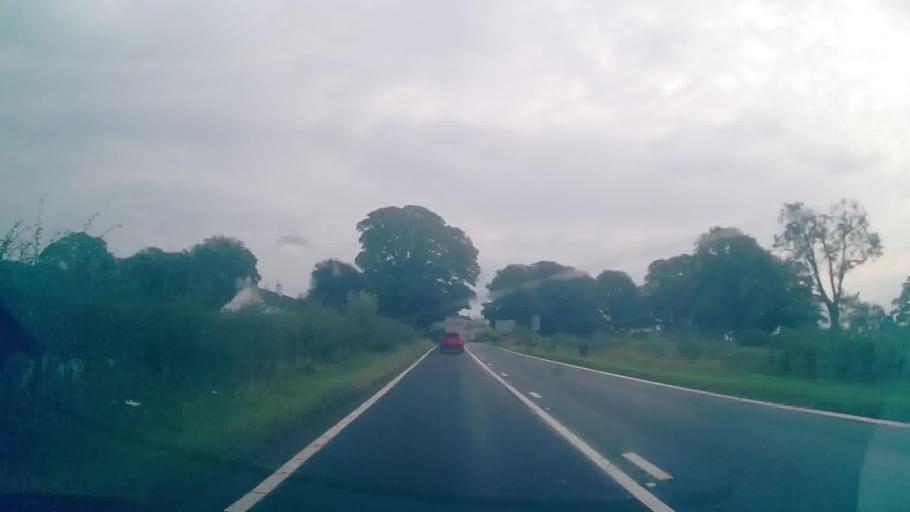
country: GB
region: Scotland
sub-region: Dumfries and Galloway
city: Lochmaben
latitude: 55.0596
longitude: -3.4782
